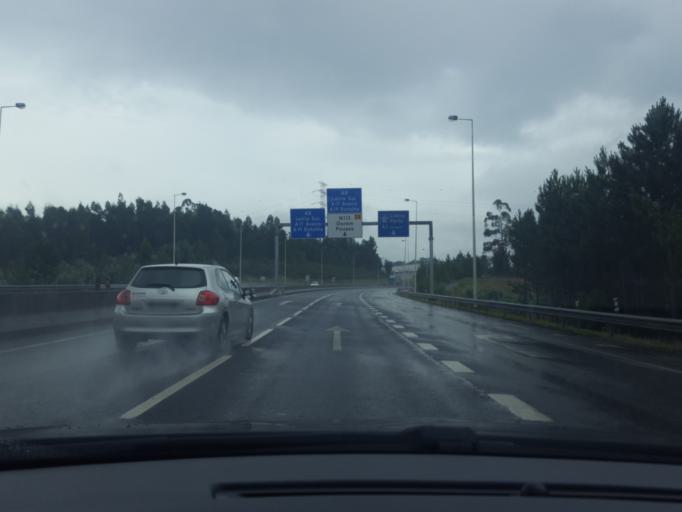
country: PT
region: Leiria
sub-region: Leiria
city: Leiria
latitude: 39.7439
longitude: -8.7707
